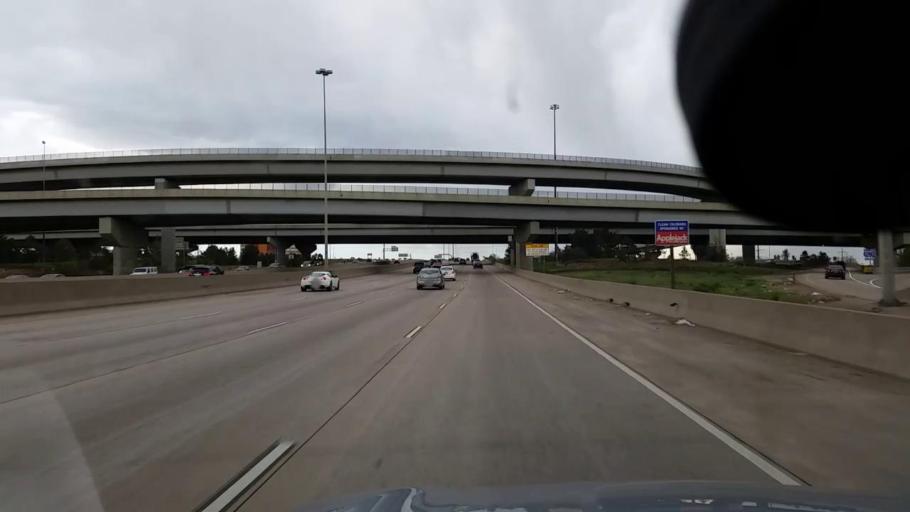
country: US
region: Colorado
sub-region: Denver County
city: Denver
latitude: 39.7783
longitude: -104.9892
